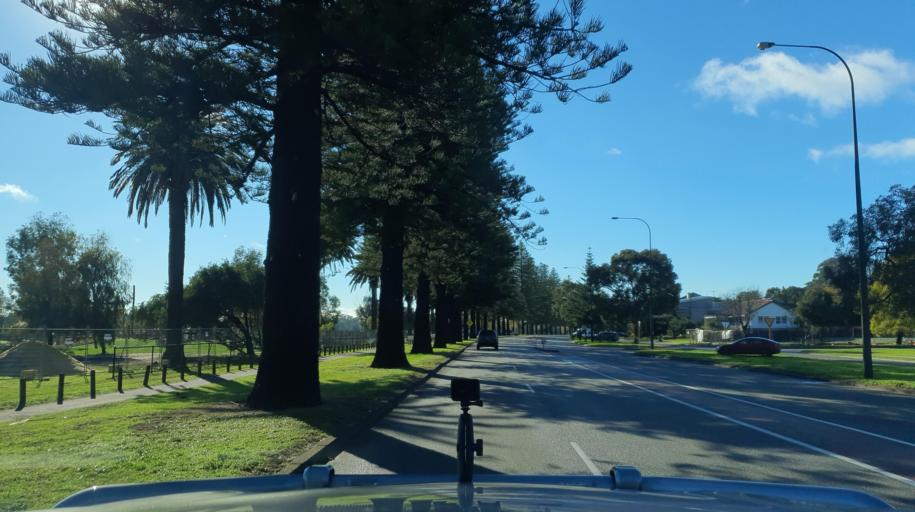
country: AU
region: Western Australia
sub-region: Cambridge
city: West Leederville
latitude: -31.9340
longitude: 115.8229
